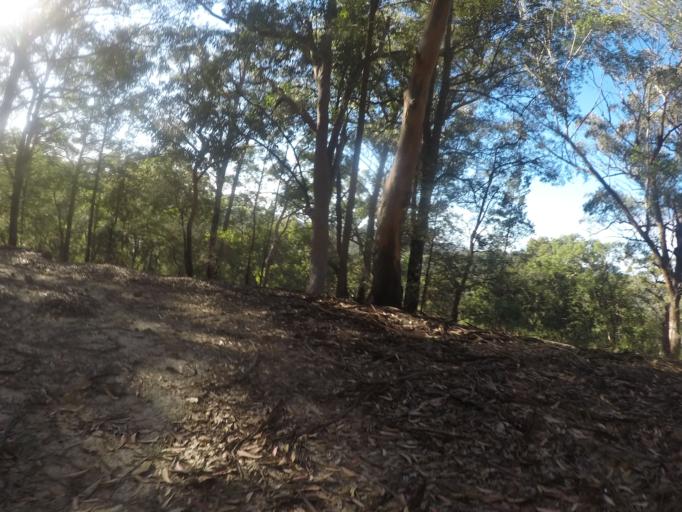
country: AU
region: New South Wales
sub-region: Hornsby Shire
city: Glenorie
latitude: -33.3514
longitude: 151.0311
